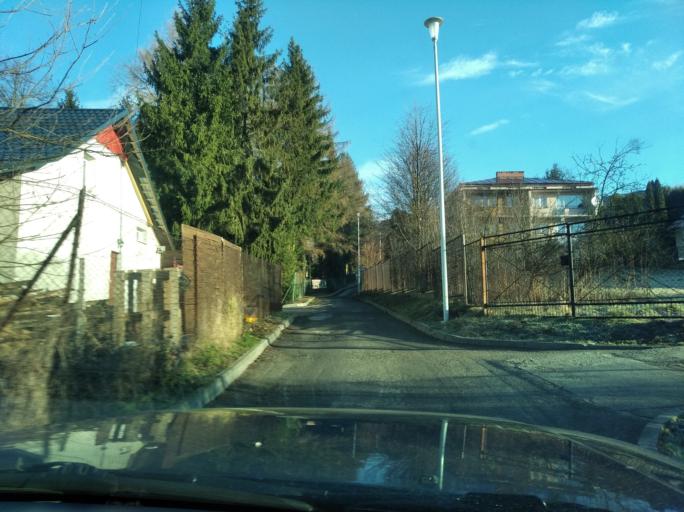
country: PL
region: Subcarpathian Voivodeship
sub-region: Powiat strzyzowski
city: Strzyzow
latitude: 49.8712
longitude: 21.8047
